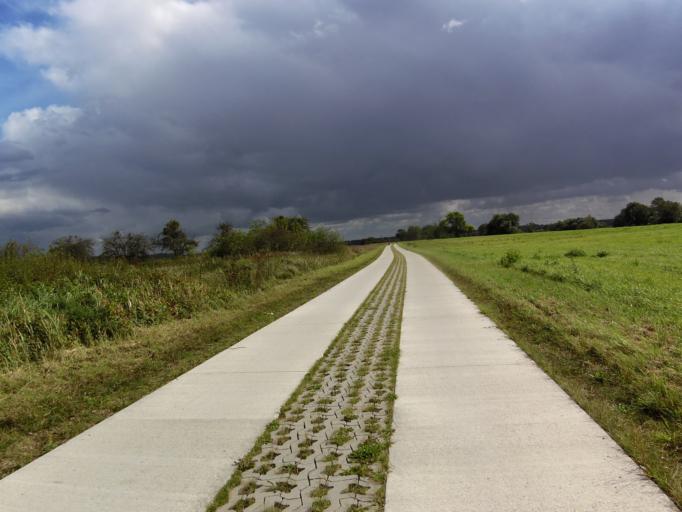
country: DE
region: Saxony-Anhalt
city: Barby
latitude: 51.9692
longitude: 11.9028
